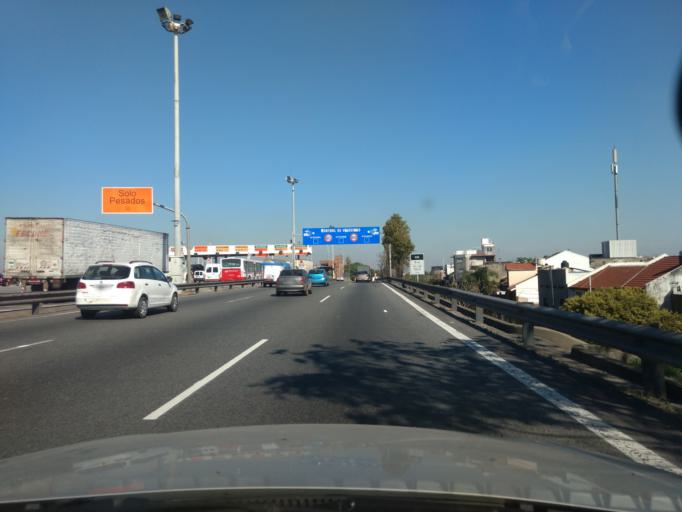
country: AR
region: Buenos Aires F.D.
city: Villa Lugano
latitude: -34.6469
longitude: -58.4638
